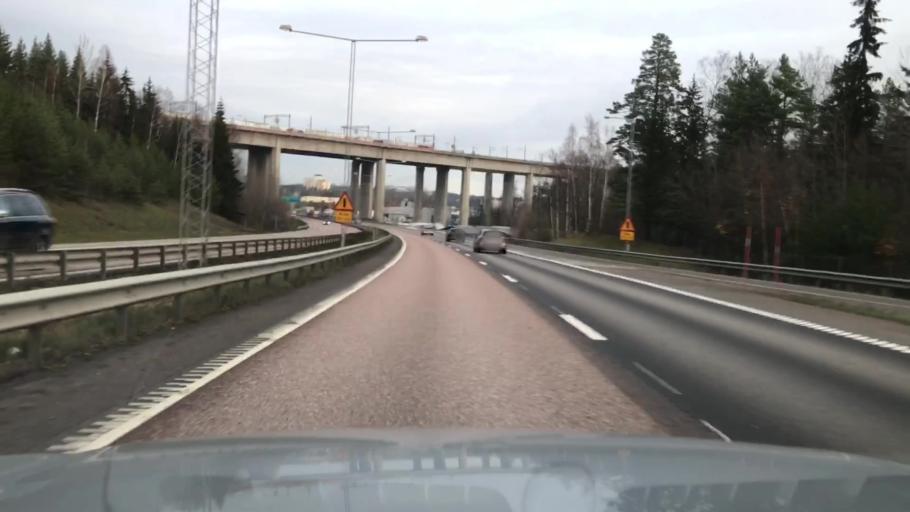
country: SE
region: Stockholm
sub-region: Sodertalje Kommun
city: Pershagen
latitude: 59.1606
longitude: 17.6483
